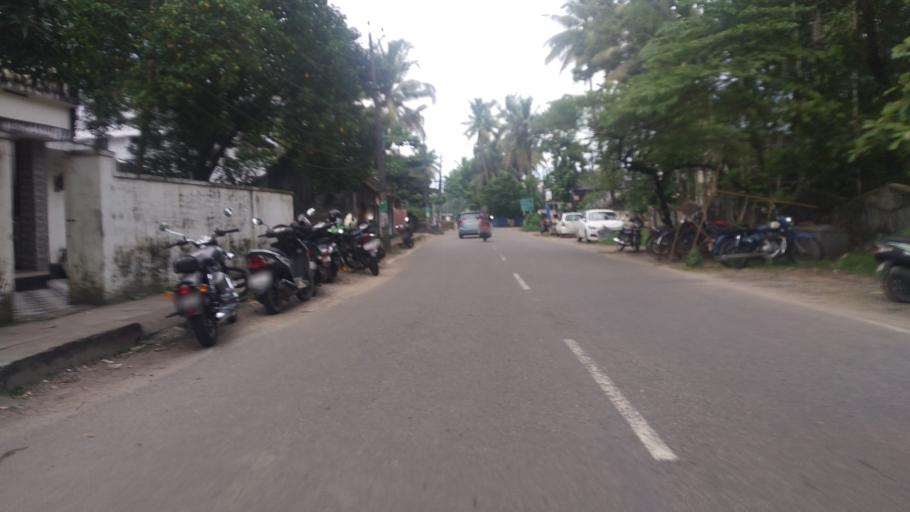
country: IN
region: Kerala
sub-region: Ernakulam
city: Cochin
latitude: 9.9326
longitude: 76.2469
